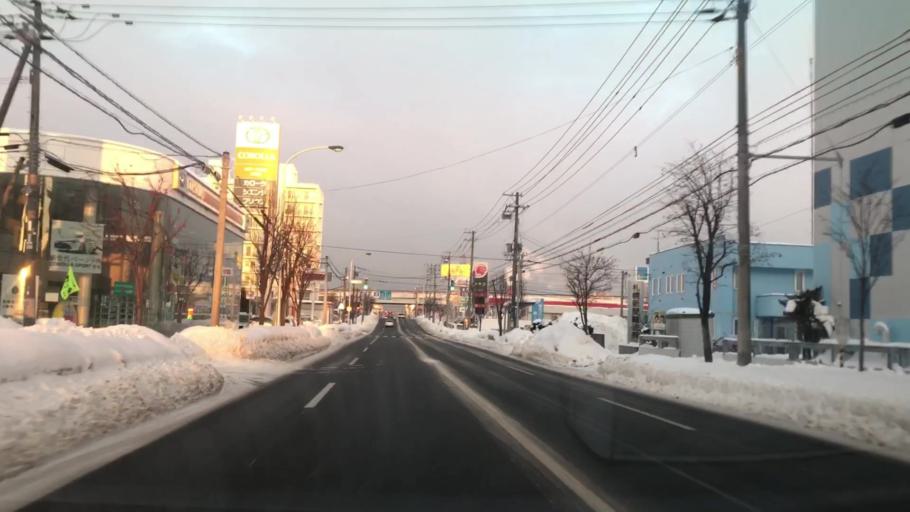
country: JP
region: Hokkaido
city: Sapporo
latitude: 43.0952
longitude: 141.3010
